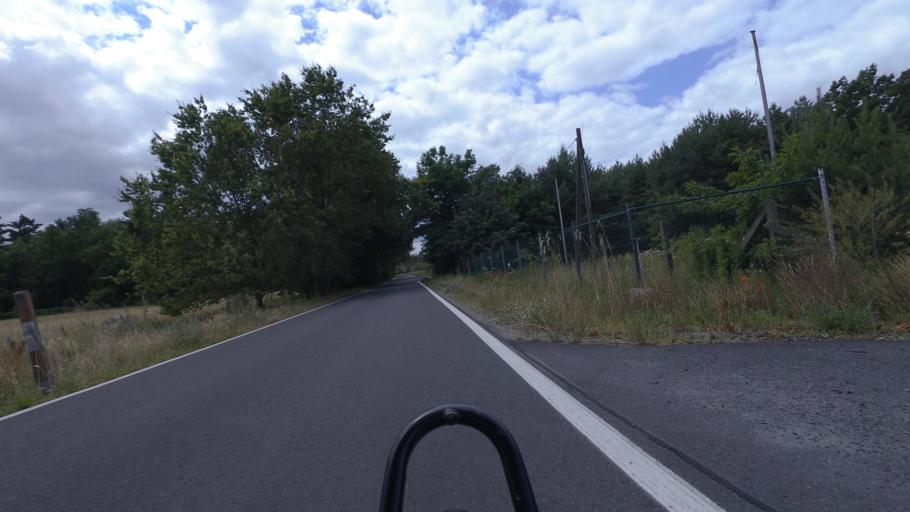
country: DE
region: Brandenburg
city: Ludwigsfelde
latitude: 52.2496
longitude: 13.2957
